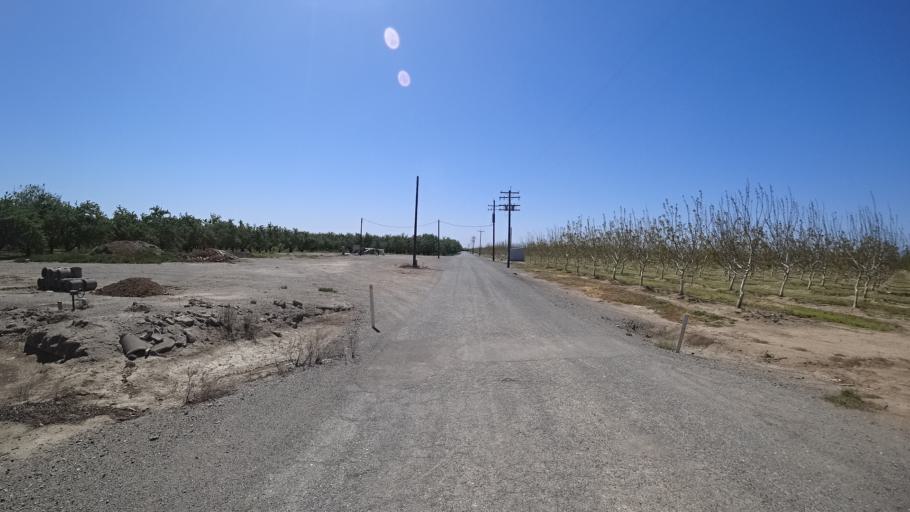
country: US
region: California
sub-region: Glenn County
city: Orland
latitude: 39.7017
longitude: -122.1546
